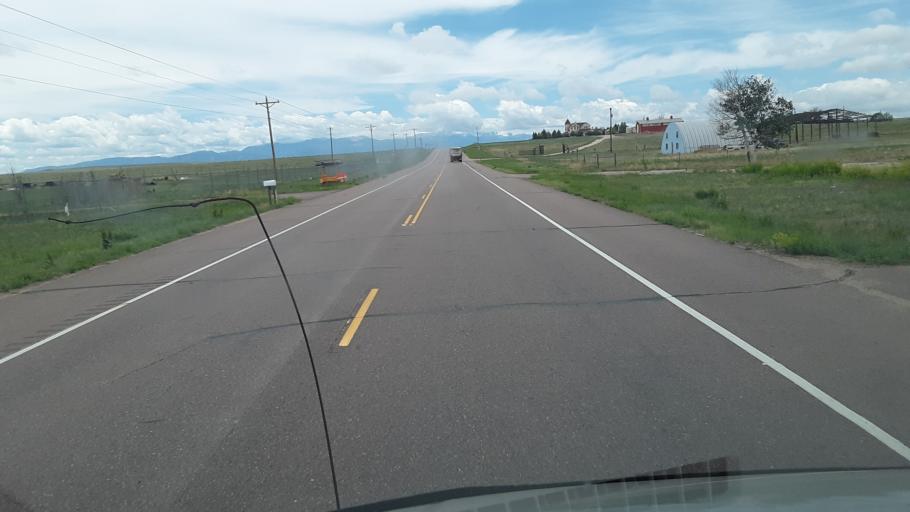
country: US
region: Colorado
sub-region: El Paso County
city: Ellicott
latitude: 38.8387
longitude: -104.4960
